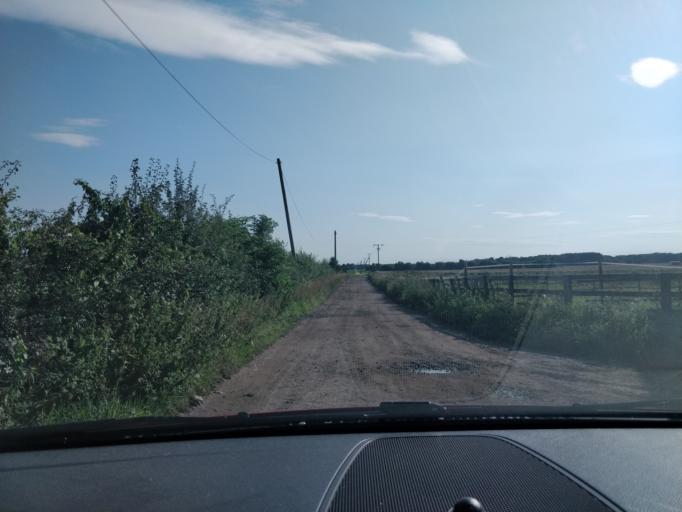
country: GB
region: England
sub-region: Lancashire
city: Banks
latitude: 53.6487
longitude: -2.9041
